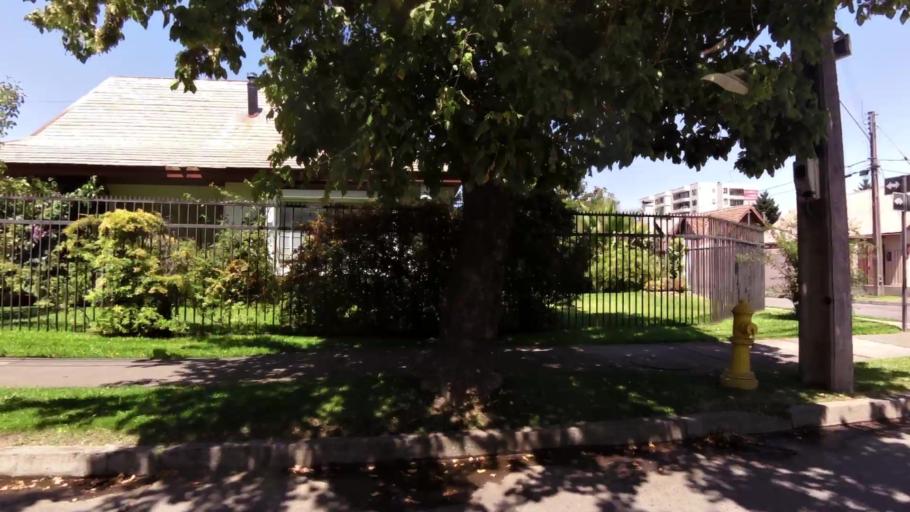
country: CL
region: Maule
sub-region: Provincia de Curico
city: Curico
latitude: -34.9874
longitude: -71.2304
